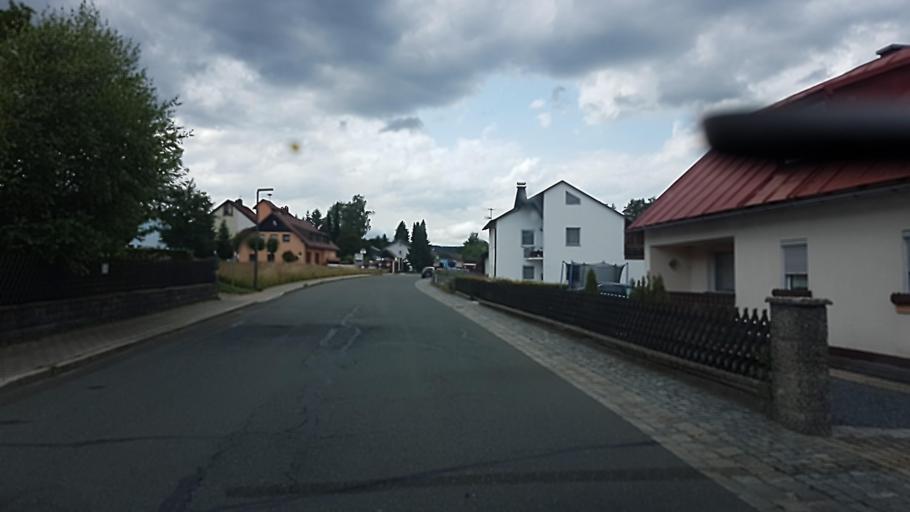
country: DE
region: Bavaria
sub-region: Upper Franconia
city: Mehlmeisel
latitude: 49.9746
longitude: 11.8717
